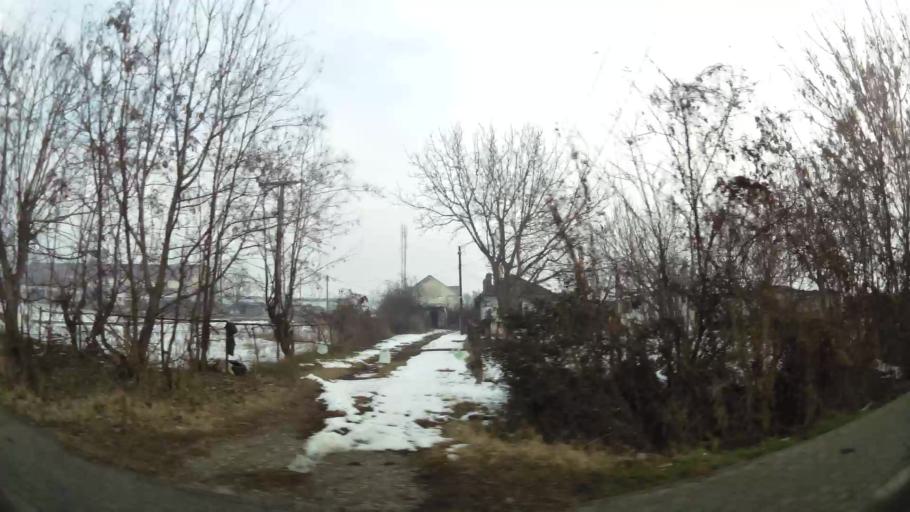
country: MK
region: Kisela Voda
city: Kisela Voda
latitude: 41.9856
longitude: 21.5194
